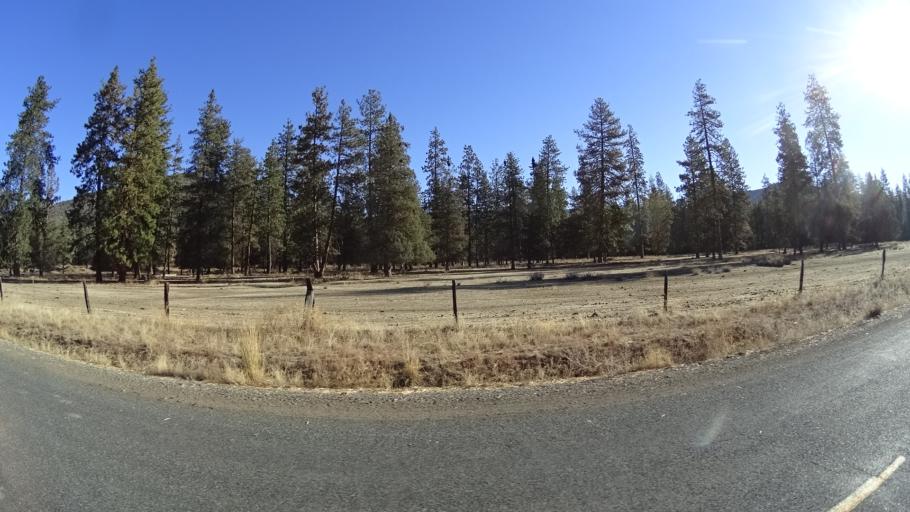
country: US
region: California
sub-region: Siskiyou County
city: Yreka
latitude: 41.4992
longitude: -122.8287
